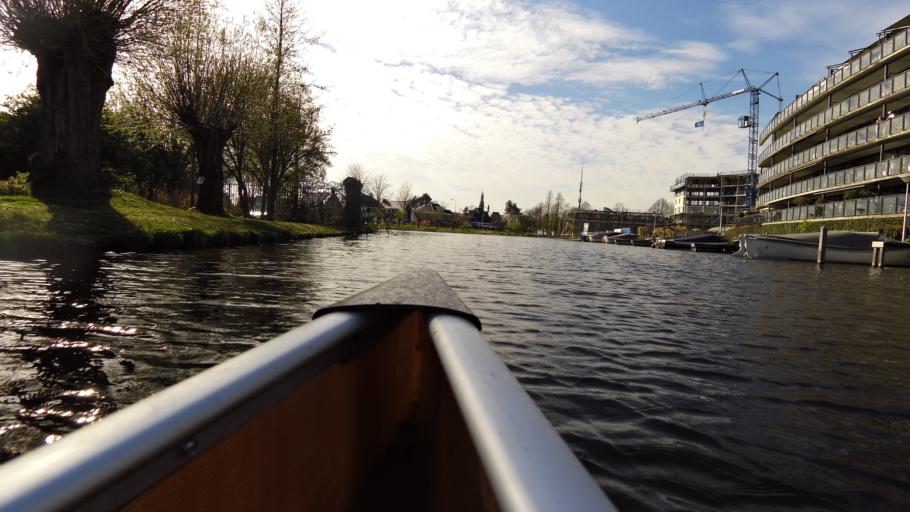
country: NL
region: South Holland
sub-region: Gemeente Lisse
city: Lisse
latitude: 52.2542
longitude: 4.5607
